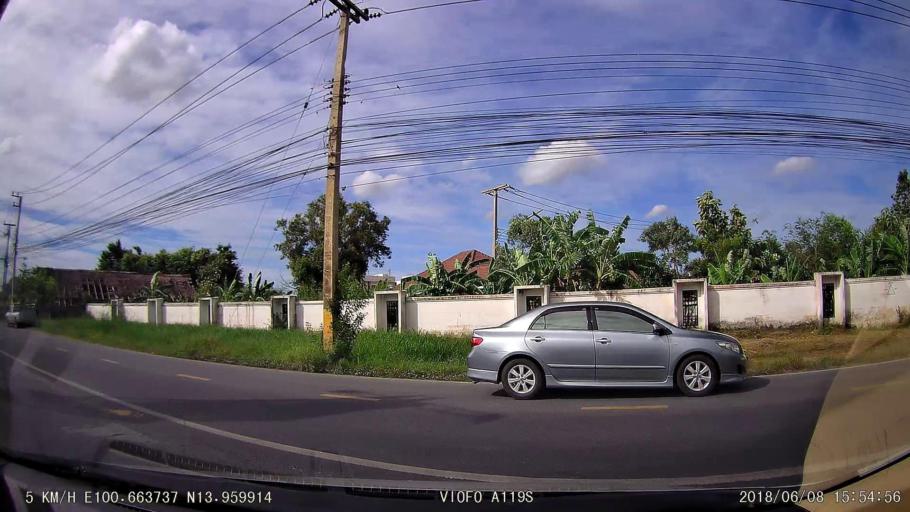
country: TH
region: Bangkok
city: Sai Mai
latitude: 13.9598
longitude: 100.6637
